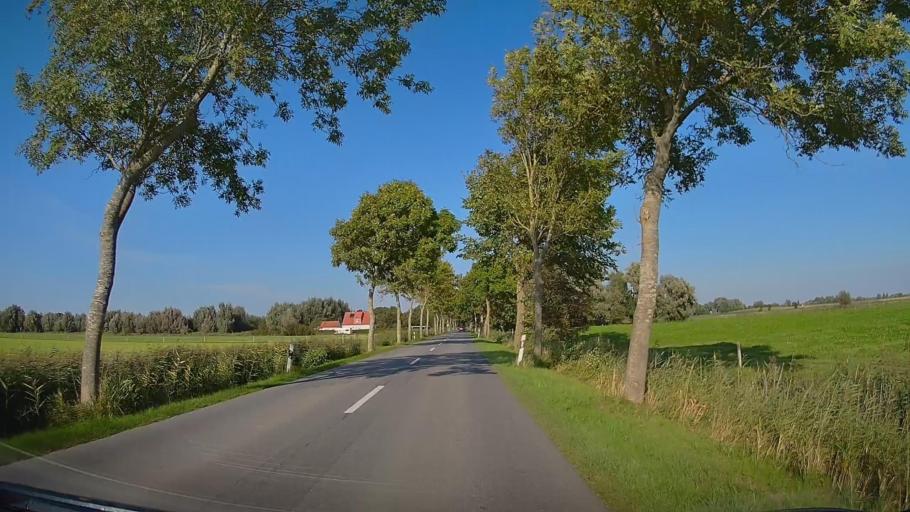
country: DE
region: Lower Saxony
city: Padingbuttel
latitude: 53.7324
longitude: 8.5450
